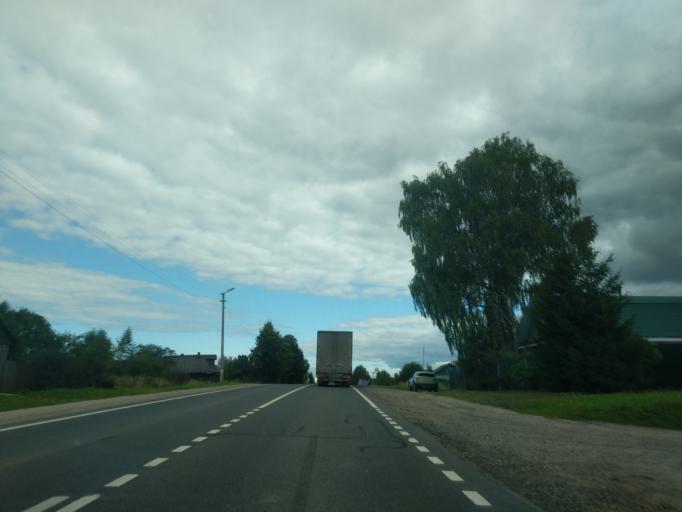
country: RU
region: Kostroma
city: Ostrovskoye
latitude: 57.8219
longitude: 42.1950
